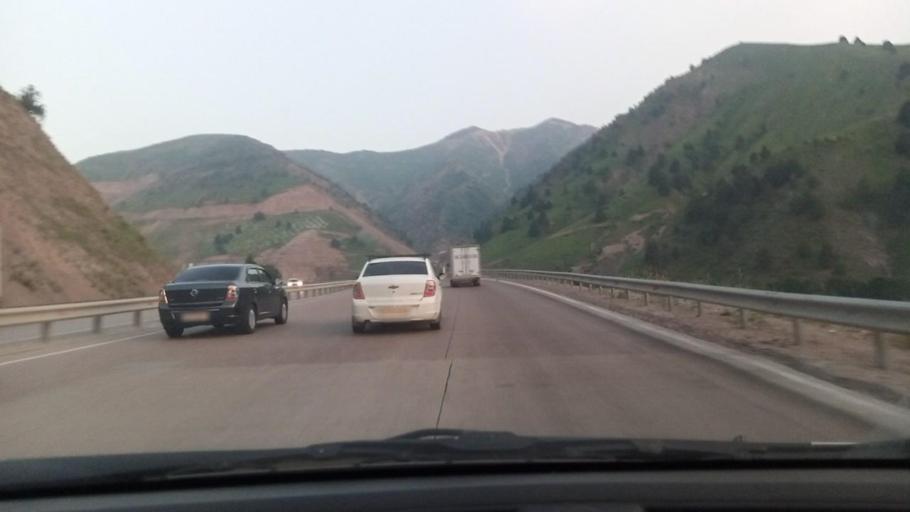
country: UZ
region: Toshkent
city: Angren
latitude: 41.1141
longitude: 70.4969
